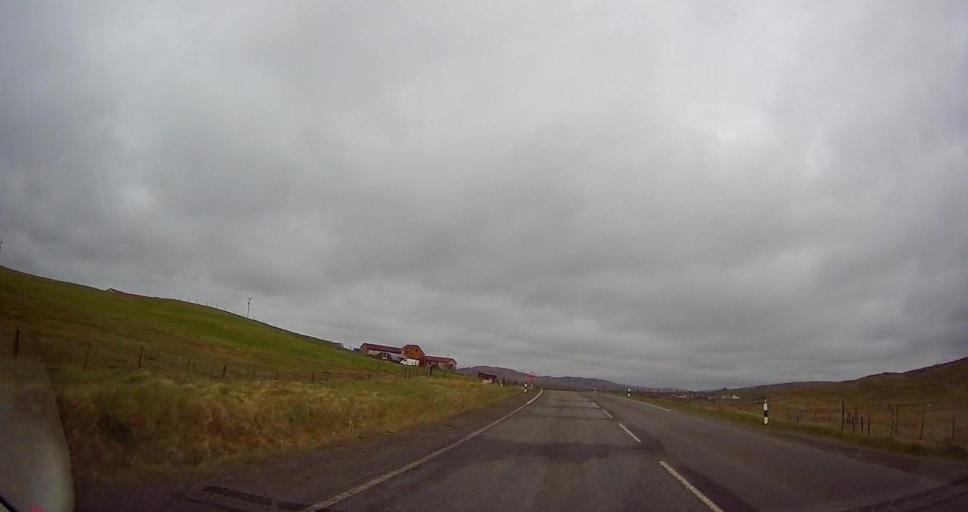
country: GB
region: Scotland
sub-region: Shetland Islands
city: Lerwick
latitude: 60.3779
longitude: -1.3401
